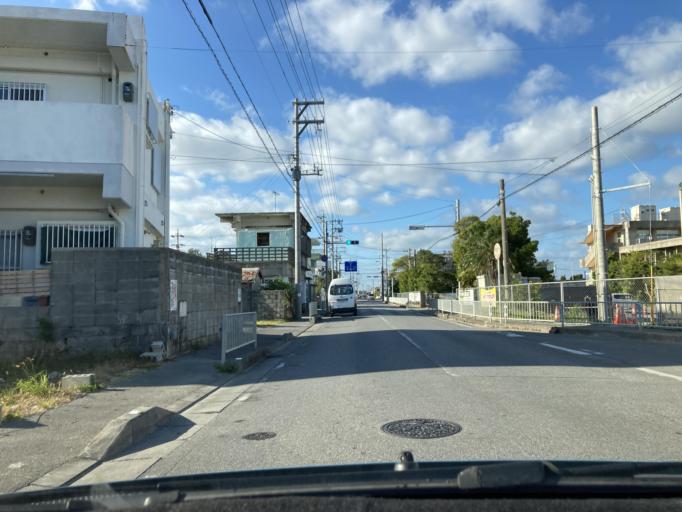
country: JP
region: Okinawa
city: Katsuren-haebaru
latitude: 26.3268
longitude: 127.9025
